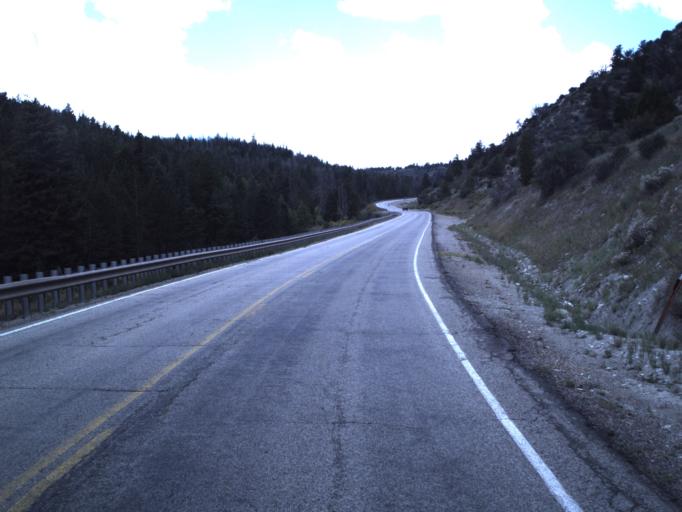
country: US
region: Utah
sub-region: Carbon County
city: Helper
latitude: 39.9035
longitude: -110.7200
